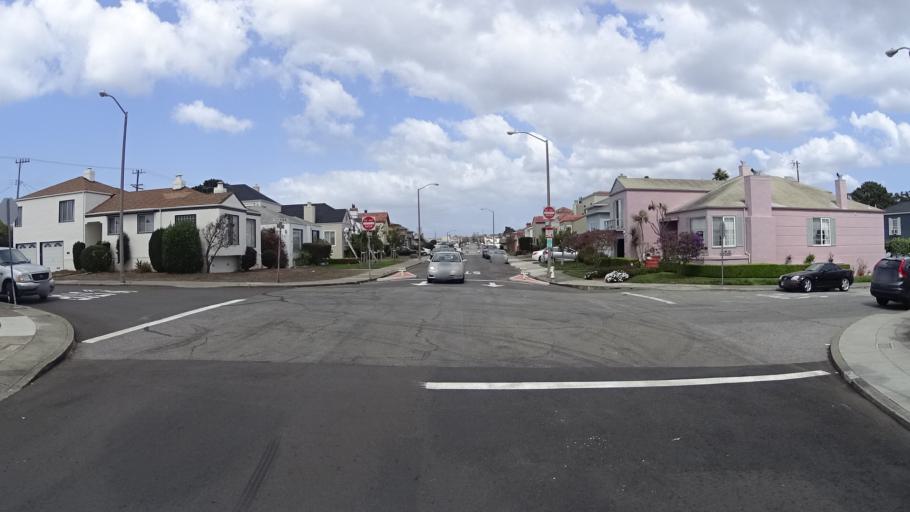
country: US
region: California
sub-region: San Mateo County
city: Daly City
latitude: 37.7352
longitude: -122.4914
